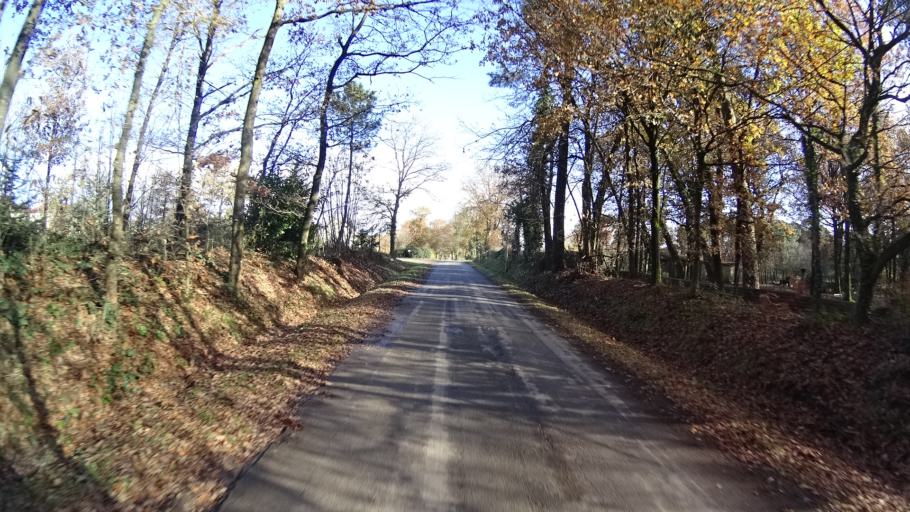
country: FR
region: Brittany
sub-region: Departement du Morbihan
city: Carentoir
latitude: 47.8289
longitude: -2.0945
